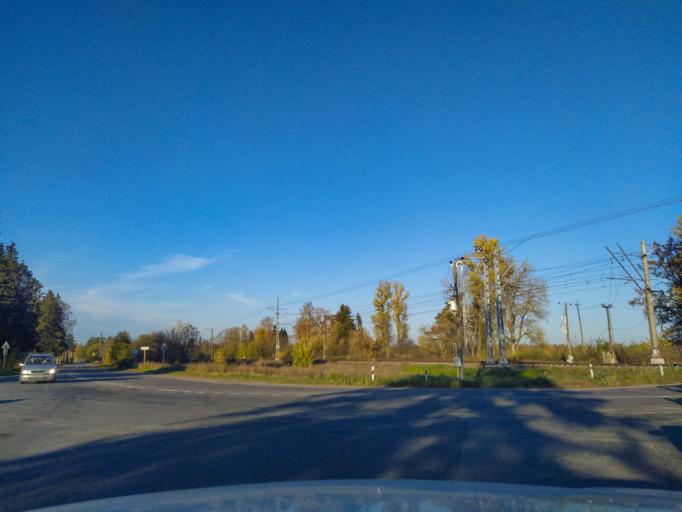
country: RU
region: Leningrad
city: Siverskiy
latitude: 59.3341
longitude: 30.0550
